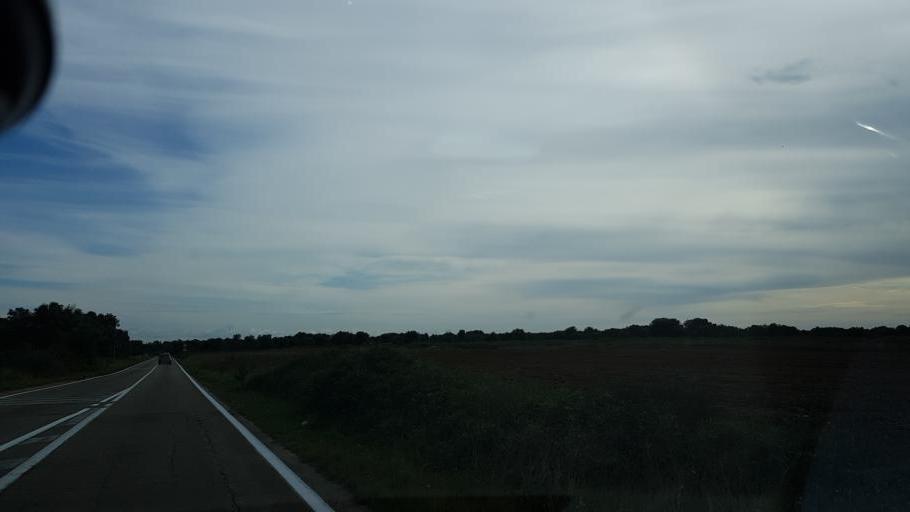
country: IT
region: Apulia
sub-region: Provincia di Lecce
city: Vernole
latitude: 40.3291
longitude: 18.3387
